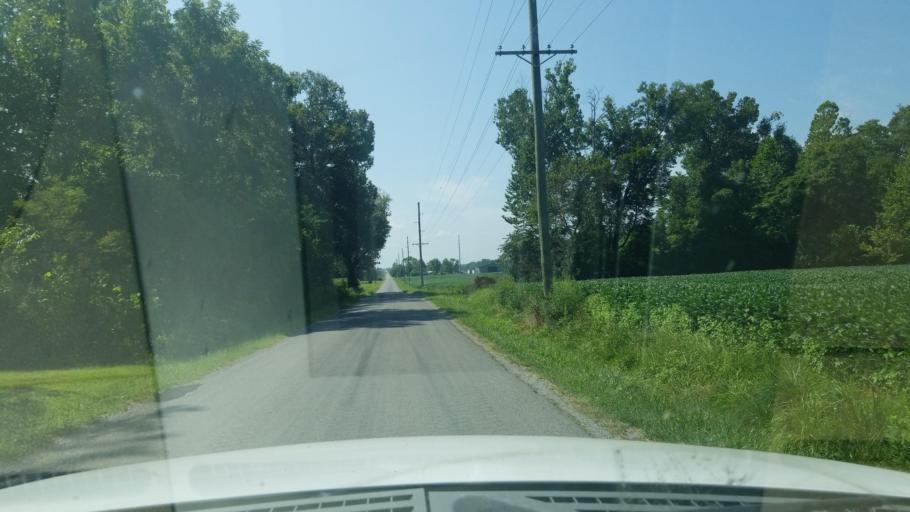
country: US
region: Illinois
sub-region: Saline County
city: Harrisburg
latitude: 37.8485
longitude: -88.6517
